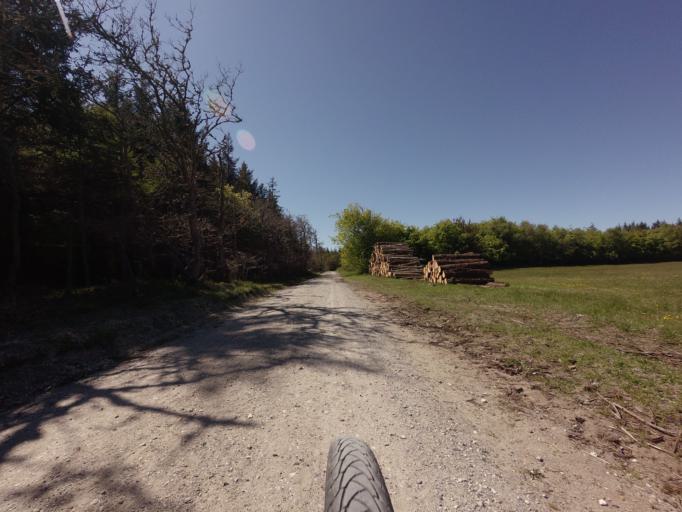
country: DK
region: North Denmark
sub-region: Jammerbugt Kommune
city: Pandrup
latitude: 57.2441
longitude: 9.5986
